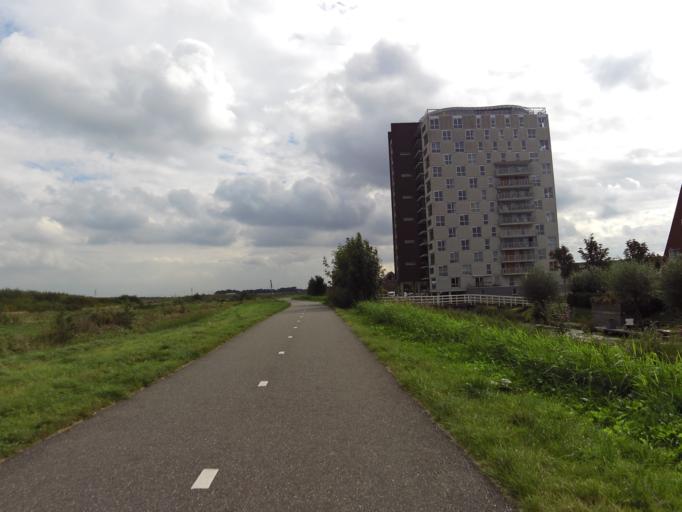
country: NL
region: South Holland
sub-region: Gemeente Rijnwoude
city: Benthuizen
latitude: 52.0705
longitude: 4.5387
